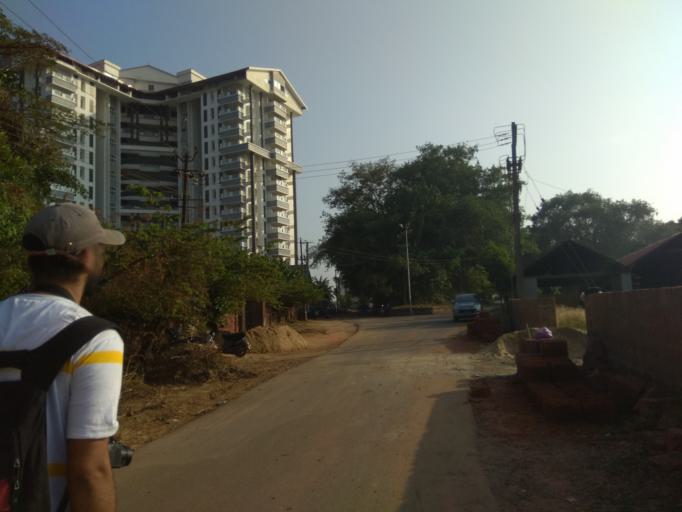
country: IN
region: Karnataka
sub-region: Dakshina Kannada
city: Ullal
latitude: 12.8449
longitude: 74.8533
